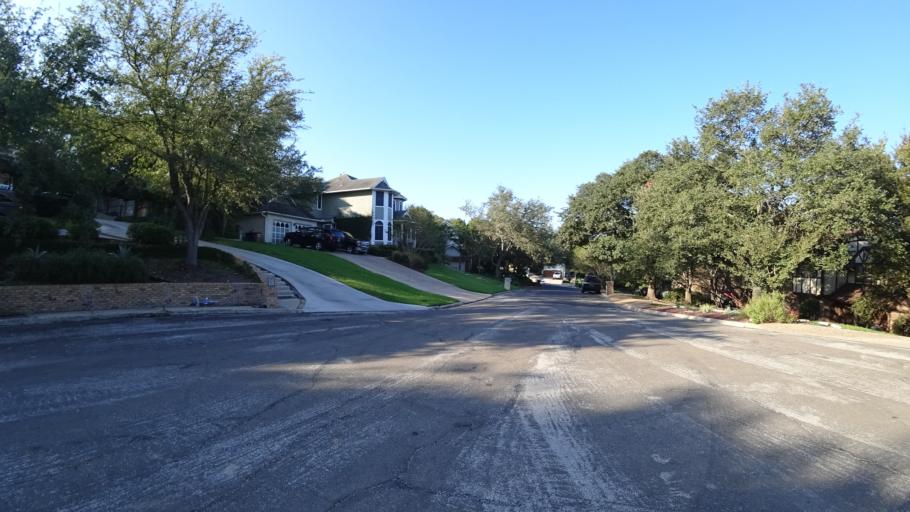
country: US
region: Texas
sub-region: Travis County
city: Rollingwood
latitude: 30.2645
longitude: -97.7984
